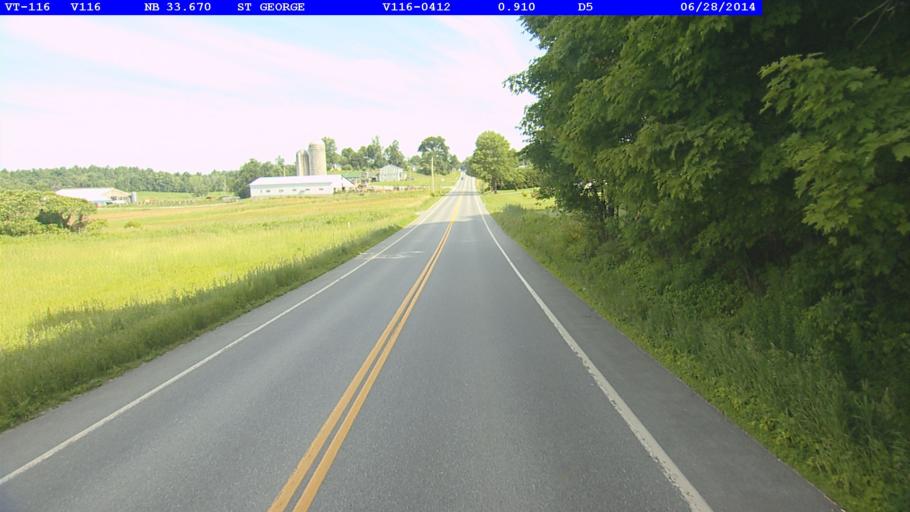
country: US
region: Vermont
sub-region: Chittenden County
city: Hinesburg
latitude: 44.3763
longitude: -73.1353
